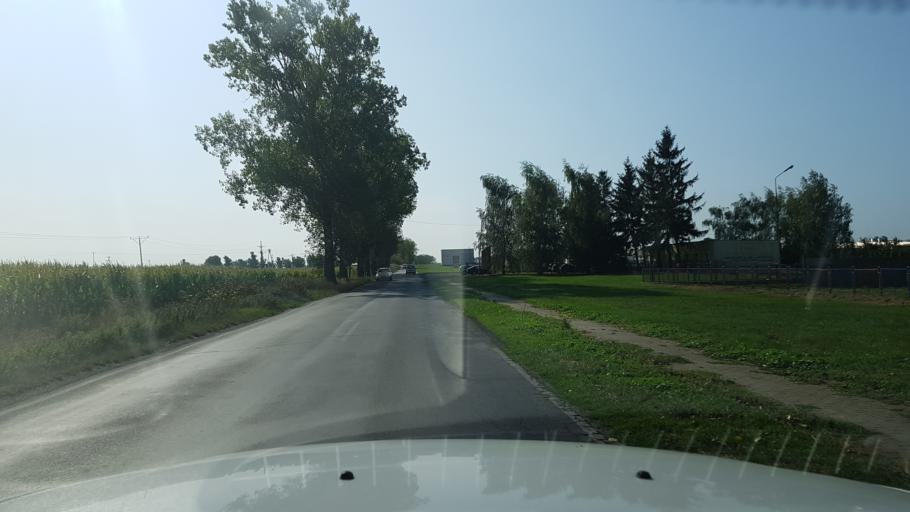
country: PL
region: West Pomeranian Voivodeship
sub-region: Powiat stargardzki
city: Stargard Szczecinski
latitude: 53.2765
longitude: 15.0817
